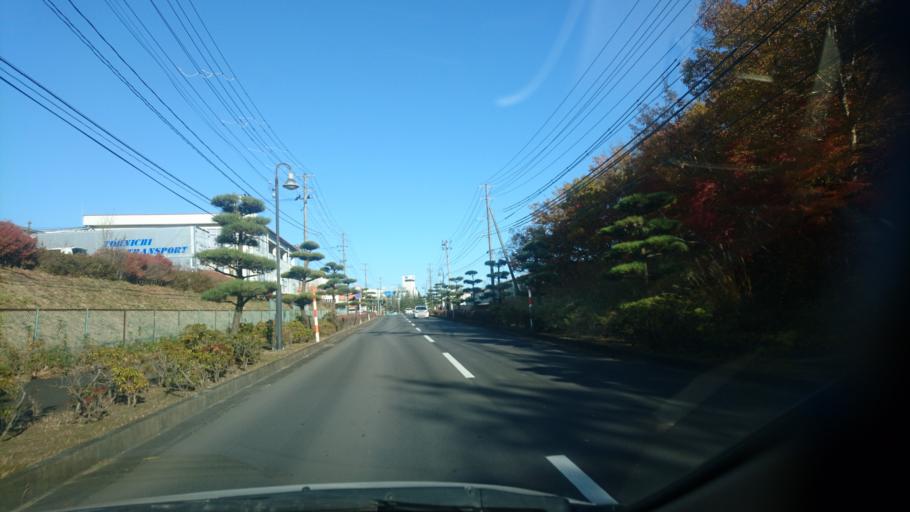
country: JP
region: Miyagi
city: Tomiya
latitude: 38.4646
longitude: 140.9183
